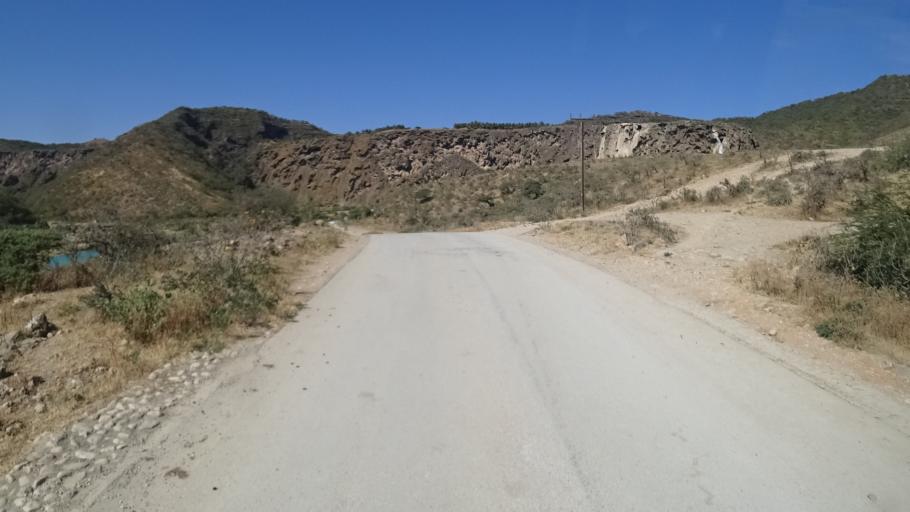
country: OM
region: Zufar
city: Salalah
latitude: 17.0716
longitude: 54.4320
